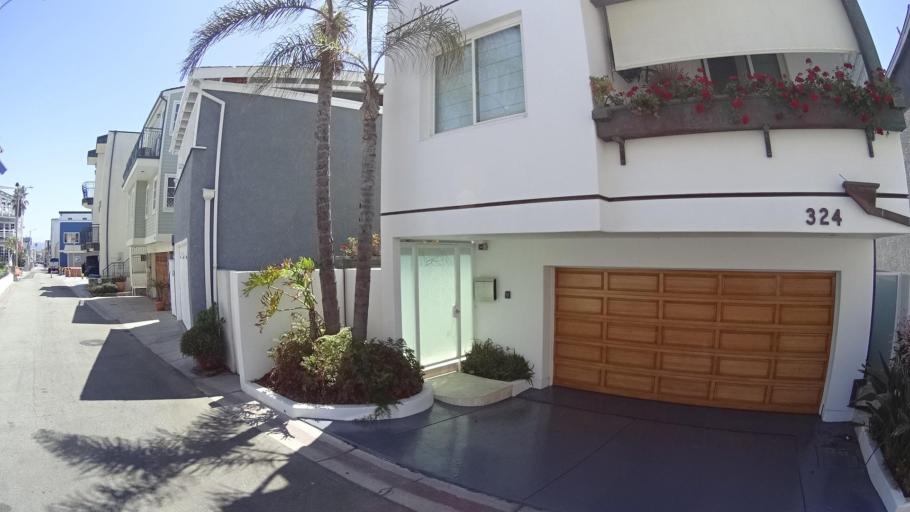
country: US
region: California
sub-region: Los Angeles County
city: Hermosa Beach
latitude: 33.8559
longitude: -118.3991
